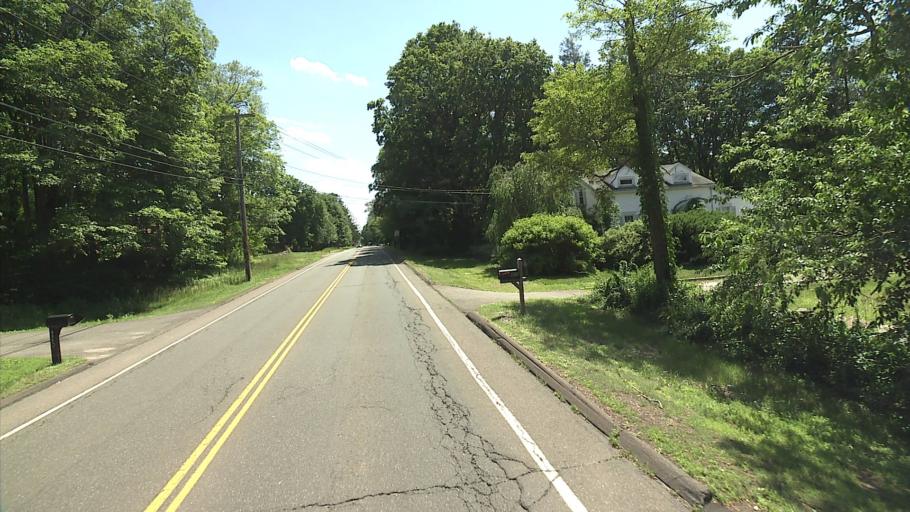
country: US
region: Connecticut
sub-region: New Haven County
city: Woodbridge
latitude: 41.3684
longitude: -72.9979
